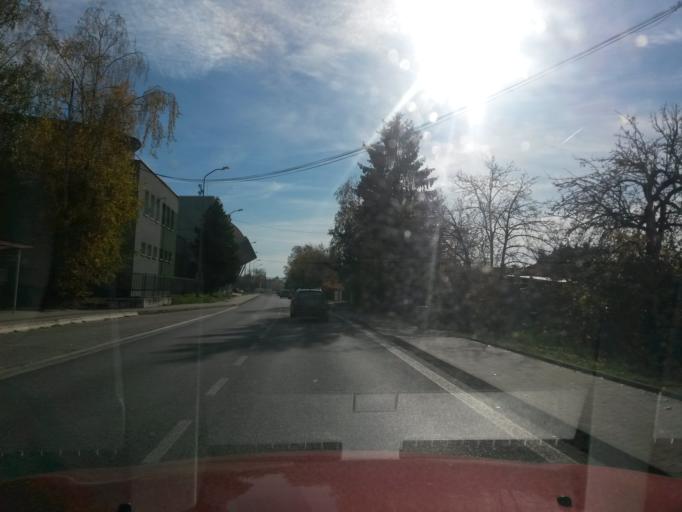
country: SK
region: Presovsky
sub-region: Okres Presov
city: Presov
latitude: 48.9963
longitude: 21.2369
